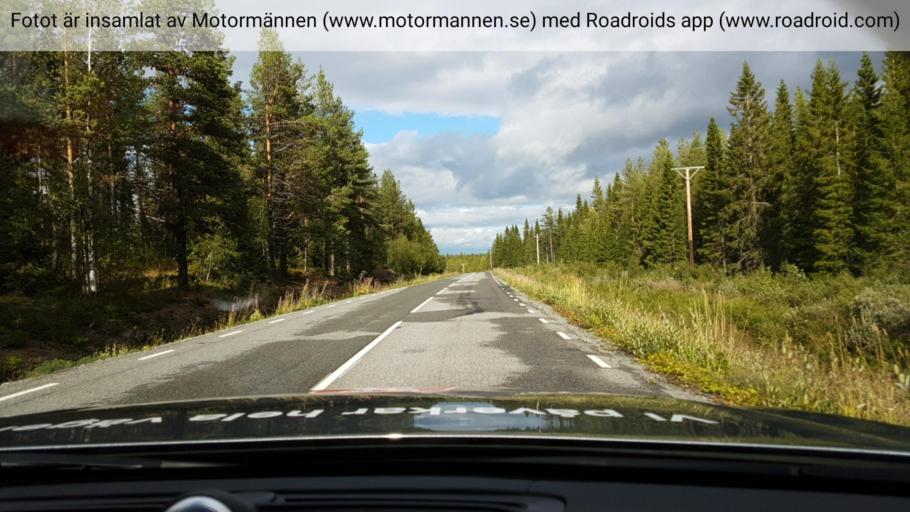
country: SE
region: Jaemtland
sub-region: Krokoms Kommun
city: Krokom
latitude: 63.6542
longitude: 14.4688
